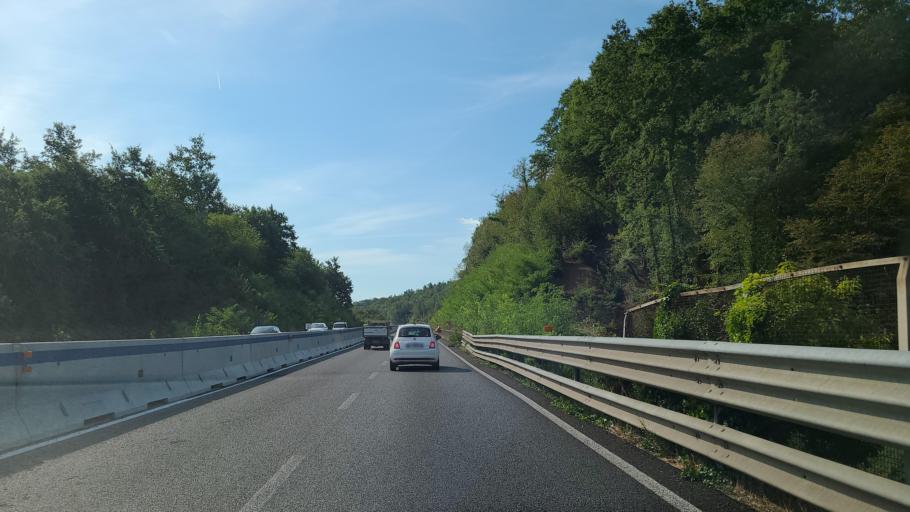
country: IT
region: Tuscany
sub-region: Province of Florence
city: Sambuca
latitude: 43.5753
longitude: 11.2054
